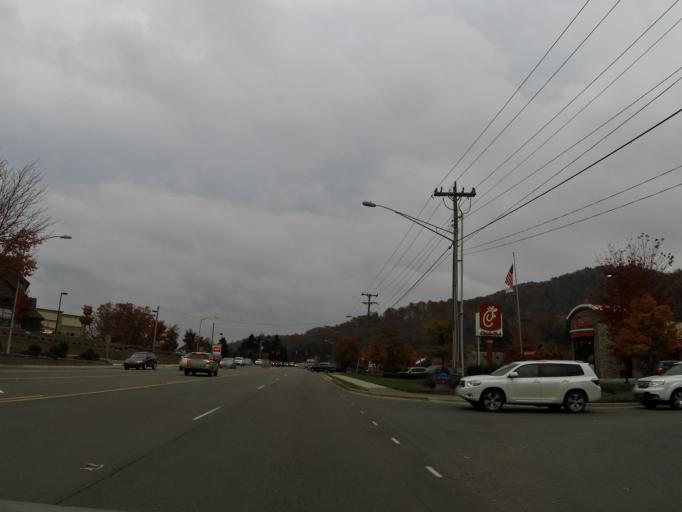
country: US
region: North Carolina
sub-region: Watauga County
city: Boone
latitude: 36.1967
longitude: -81.6547
